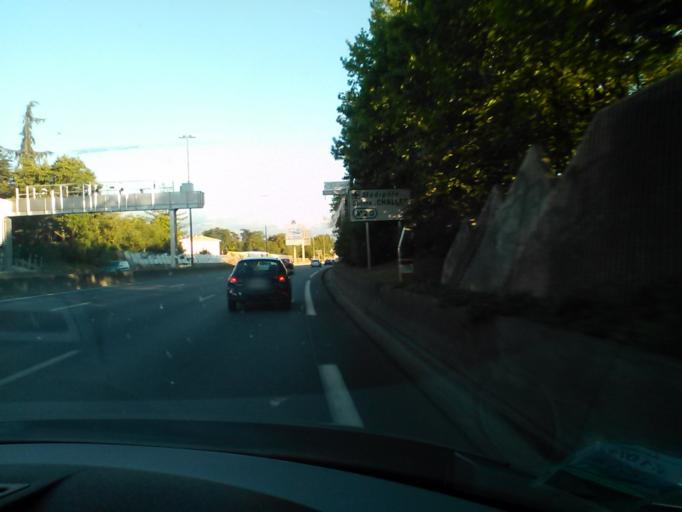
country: FR
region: Rhone-Alpes
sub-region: Departement de la Savoie
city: Chambery
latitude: 45.5658
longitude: 5.9465
